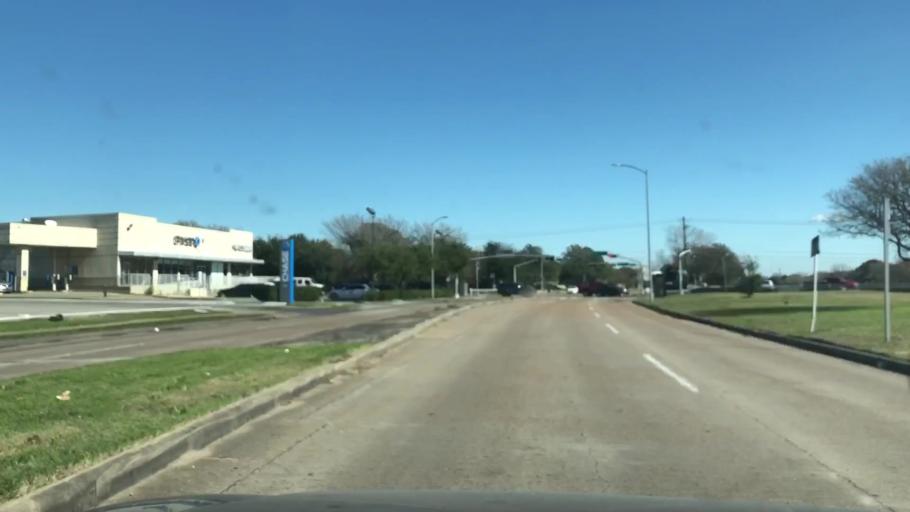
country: US
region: Texas
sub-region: Harris County
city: Bellaire
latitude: 29.6777
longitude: -95.4780
